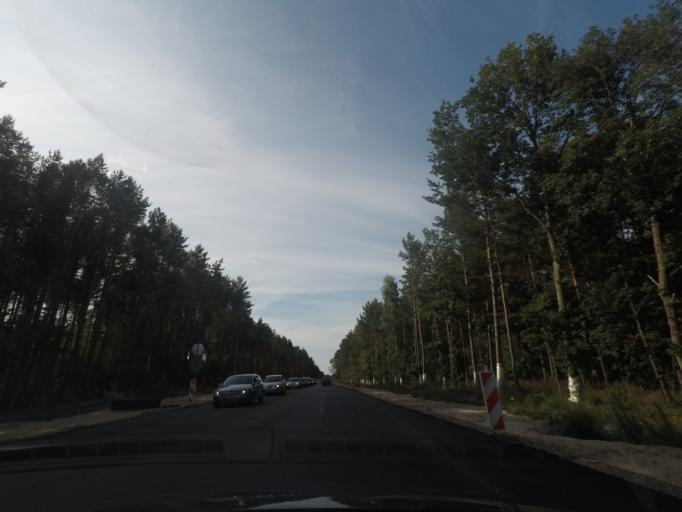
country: PL
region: Pomeranian Voivodeship
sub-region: Powiat leborski
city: Leba
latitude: 54.7152
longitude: 17.5769
